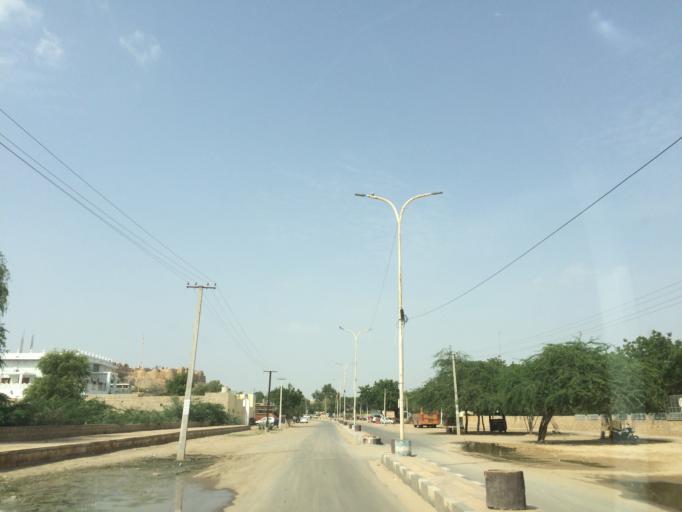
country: IN
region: Rajasthan
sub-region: Jaisalmer
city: Jaisalmer
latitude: 26.9068
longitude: 70.9107
